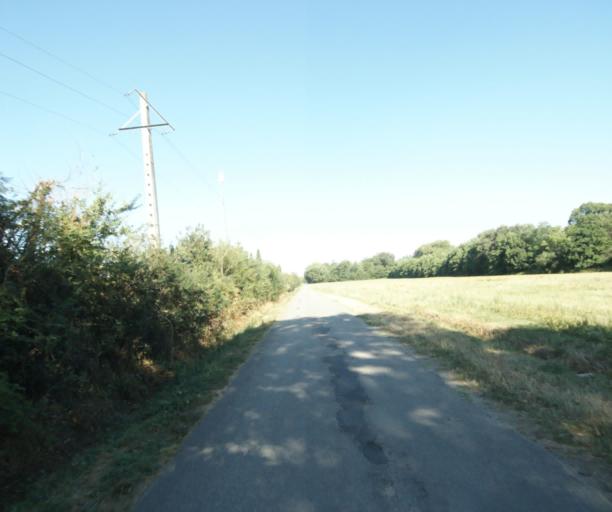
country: FR
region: Midi-Pyrenees
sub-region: Departement de la Haute-Garonne
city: Revel
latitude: 43.4637
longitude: 2.0195
